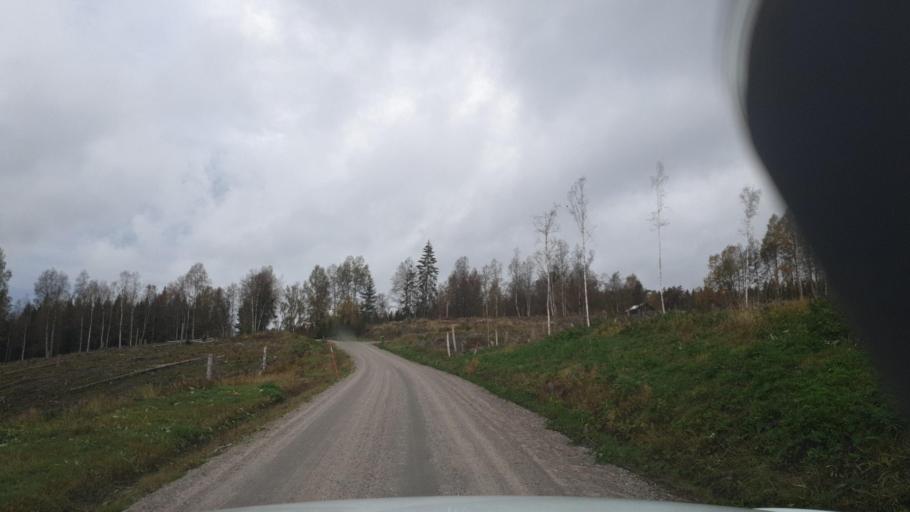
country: SE
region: Vaermland
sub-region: Arvika Kommun
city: Arvika
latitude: 59.8372
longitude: 12.8058
